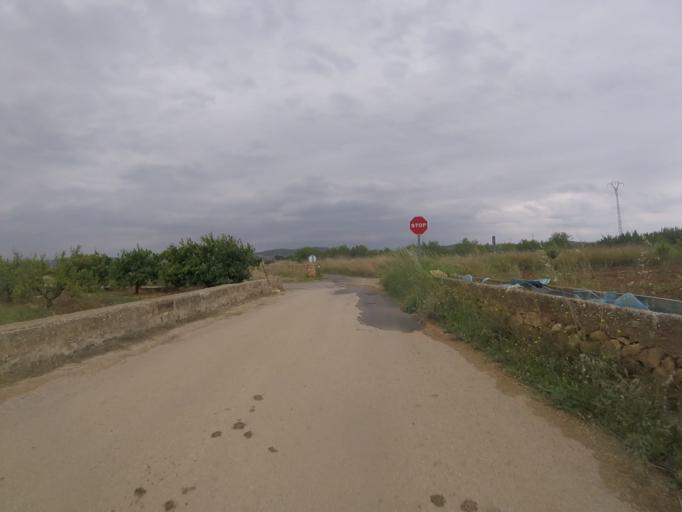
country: ES
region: Valencia
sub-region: Provincia de Castello
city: Torreblanca
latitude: 40.2186
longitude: 0.2218
